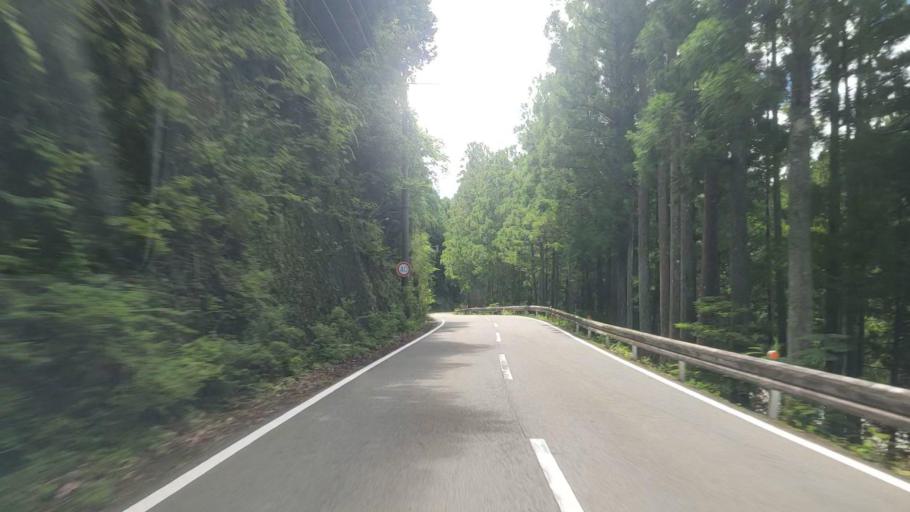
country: JP
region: Mie
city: Owase
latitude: 33.9681
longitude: 136.0615
